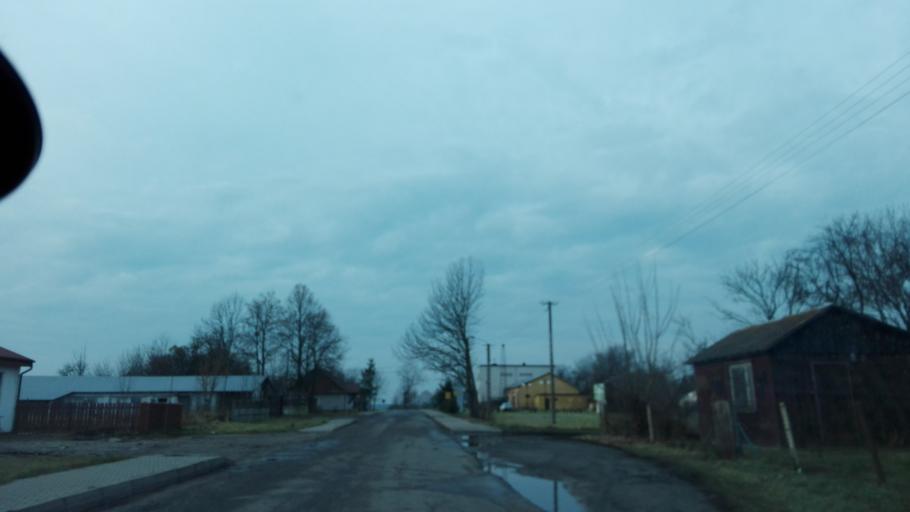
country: PL
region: Lublin Voivodeship
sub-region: Powiat bialski
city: Sosnowka
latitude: 51.7503
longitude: 23.3411
